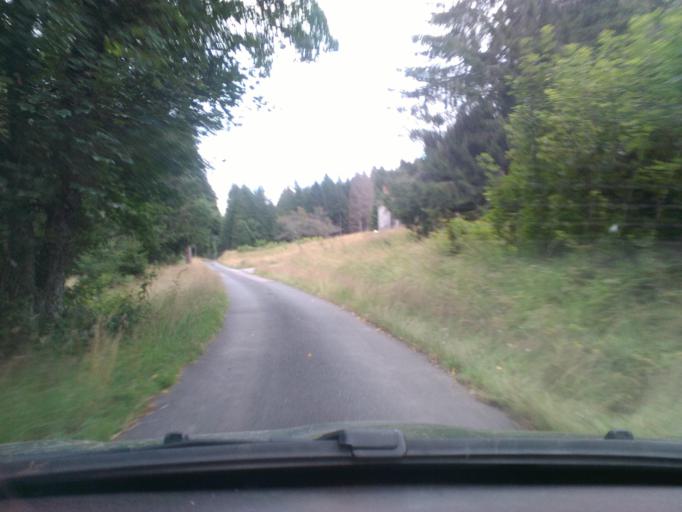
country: FR
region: Lorraine
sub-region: Departement des Vosges
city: Xonrupt-Longemer
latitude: 48.0825
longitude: 6.9541
